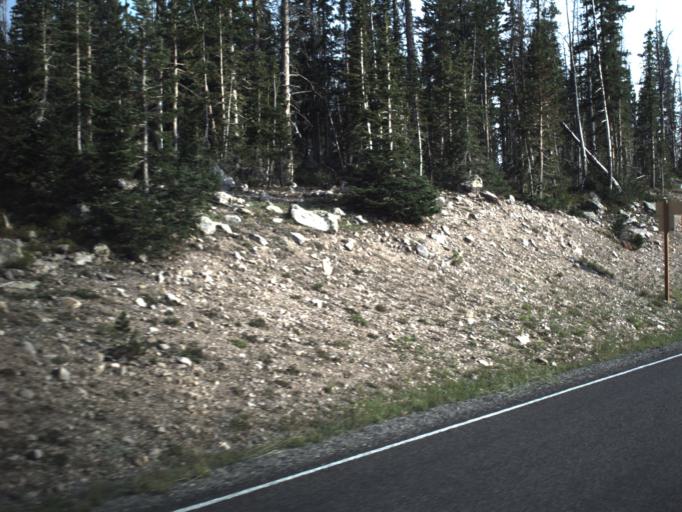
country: US
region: Utah
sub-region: Summit County
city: Kamas
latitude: 40.7226
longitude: -110.8654
